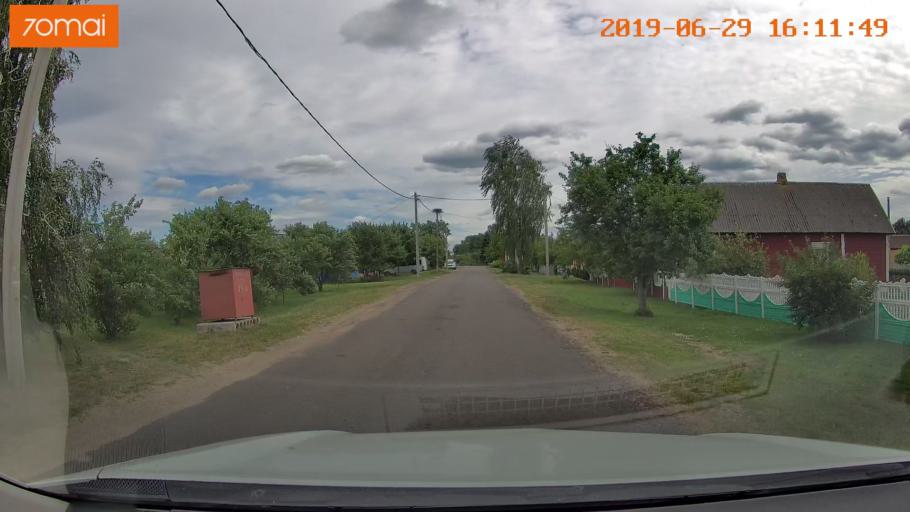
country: BY
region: Brest
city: Luninyets
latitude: 52.2032
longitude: 27.0122
